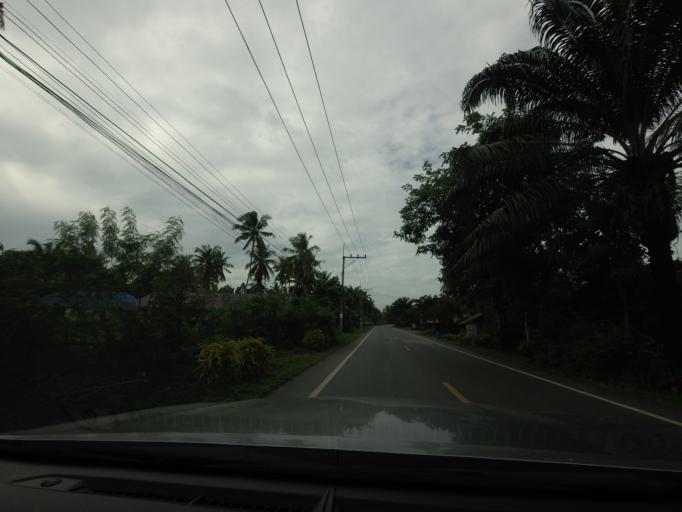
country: TH
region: Nakhon Si Thammarat
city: Phra Phrom
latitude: 8.2960
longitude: 99.9450
